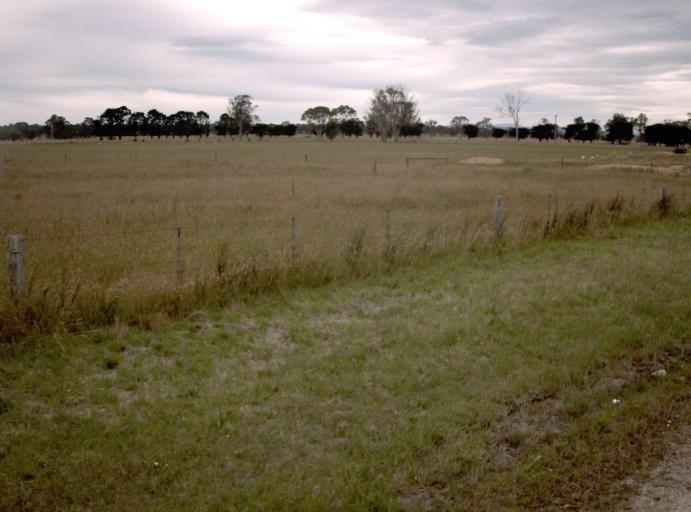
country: AU
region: Victoria
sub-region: East Gippsland
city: Bairnsdale
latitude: -37.9298
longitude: 147.5392
